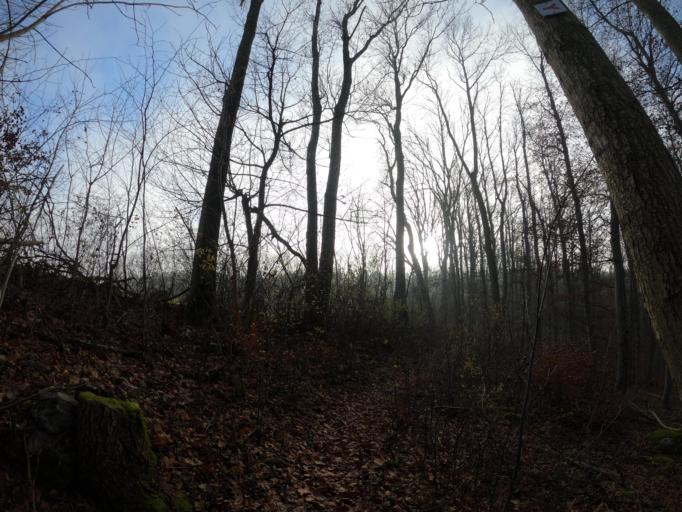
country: DE
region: Baden-Wuerttemberg
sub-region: Regierungsbezirk Stuttgart
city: Deggingen
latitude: 48.5944
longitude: 9.7439
